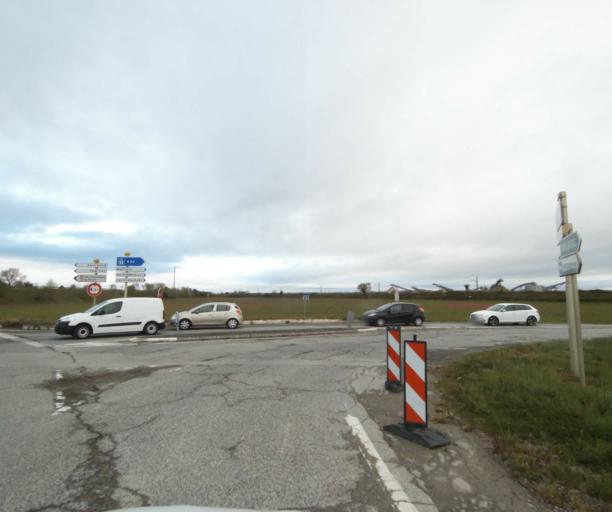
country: FR
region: Midi-Pyrenees
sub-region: Departement de l'Ariege
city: Saverdun
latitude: 43.2276
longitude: 1.6068
